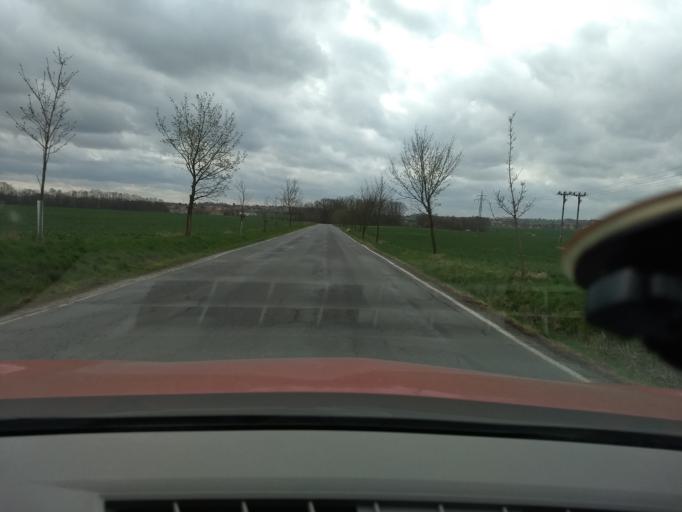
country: CZ
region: Central Bohemia
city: Unhost'
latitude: 50.0786
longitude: 14.1430
